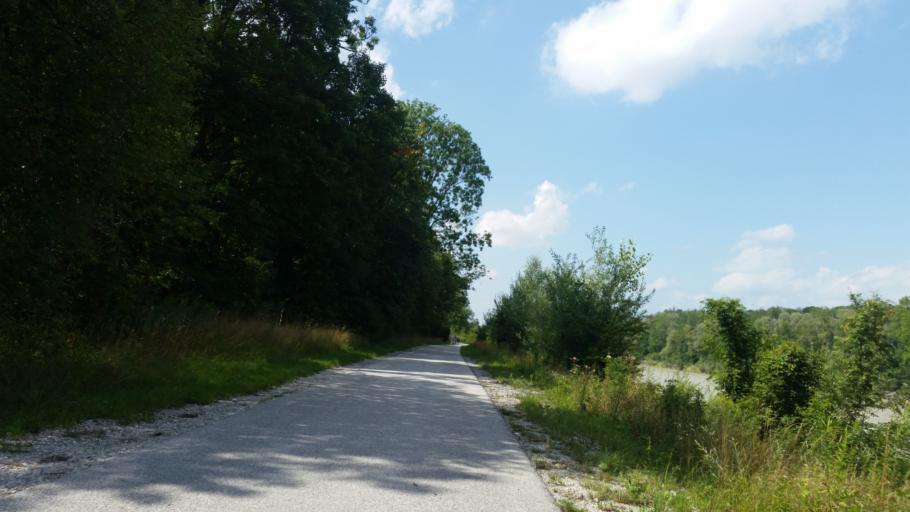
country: AT
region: Salzburg
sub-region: Politischer Bezirk Salzburg-Umgebung
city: Bergheim
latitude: 47.8455
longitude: 13.0107
